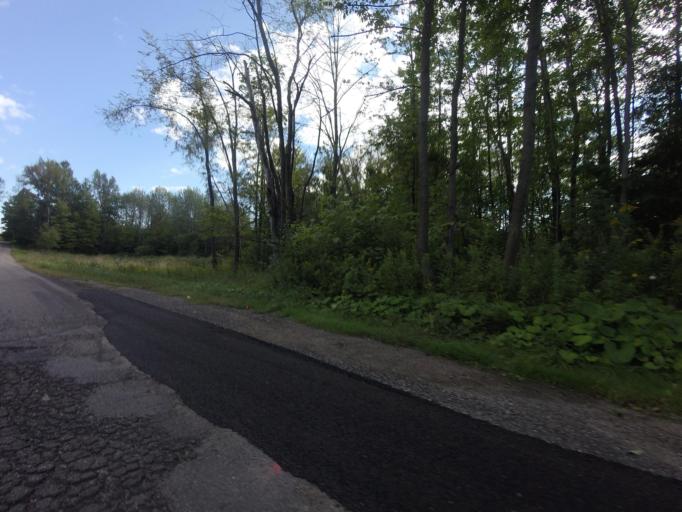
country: CA
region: Ontario
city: Orangeville
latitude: 43.8185
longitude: -79.9878
